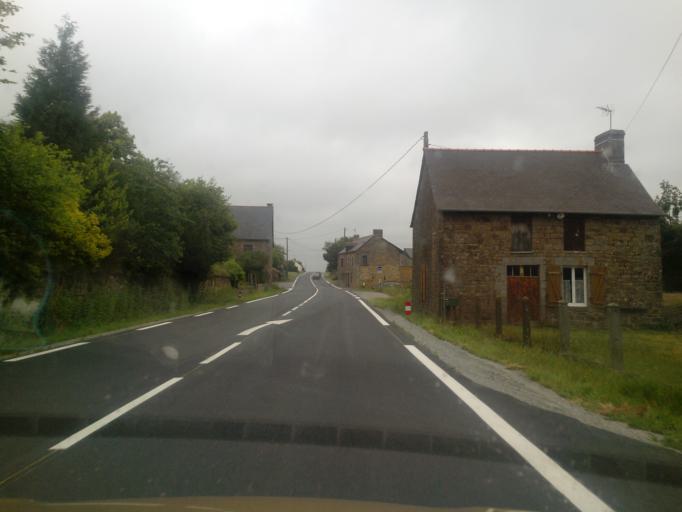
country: FR
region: Brittany
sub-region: Departement d'Ille-et-Vilaine
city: Sens-de-Bretagne
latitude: 48.3180
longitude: -1.5337
